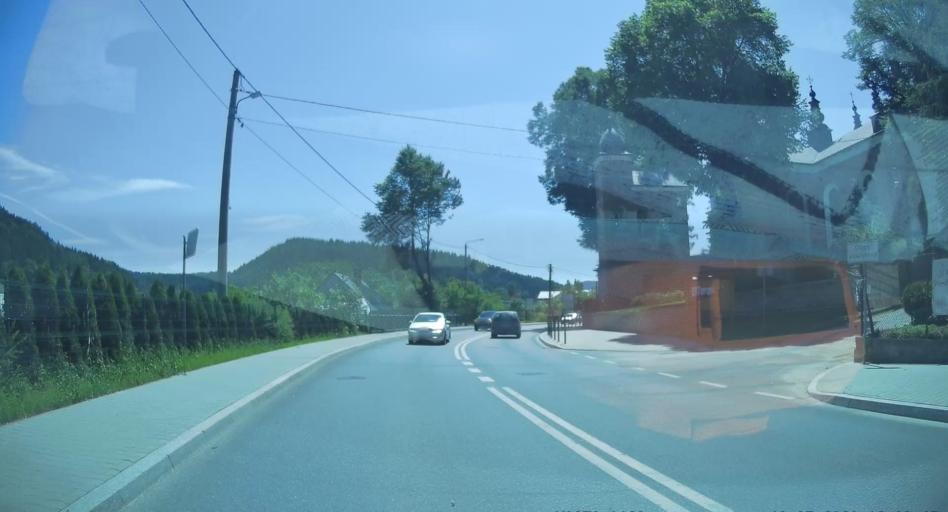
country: PL
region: Lesser Poland Voivodeship
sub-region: Powiat nowosadecki
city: Krynica-Zdroj
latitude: 49.3960
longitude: 20.9574
